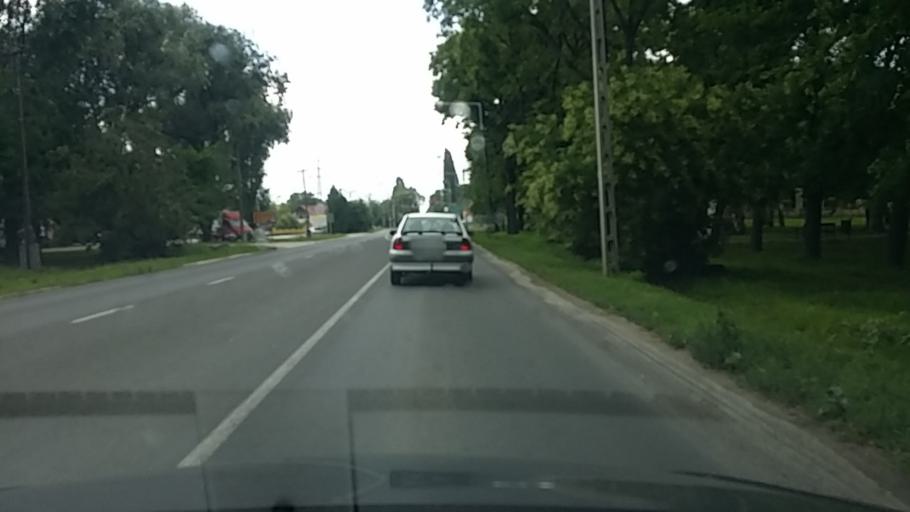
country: HU
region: Pest
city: Orkeny
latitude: 47.1262
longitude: 19.4304
